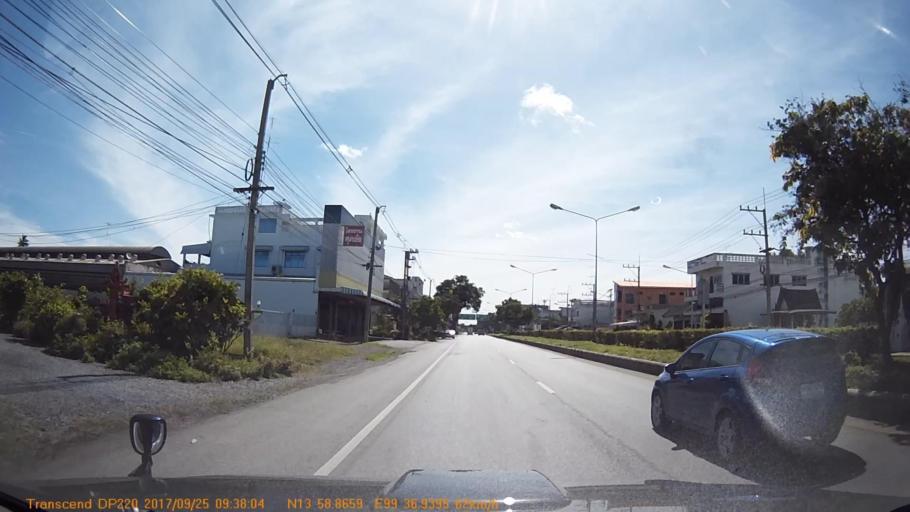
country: TH
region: Kanchanaburi
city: Tha Muang
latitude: 13.9811
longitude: 99.6157
